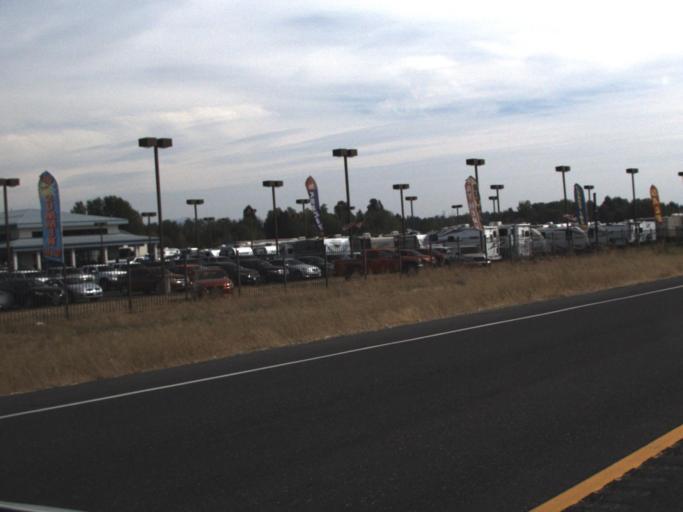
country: US
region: Washington
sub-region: Spokane County
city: Deer Park
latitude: 47.9411
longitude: -117.4758
